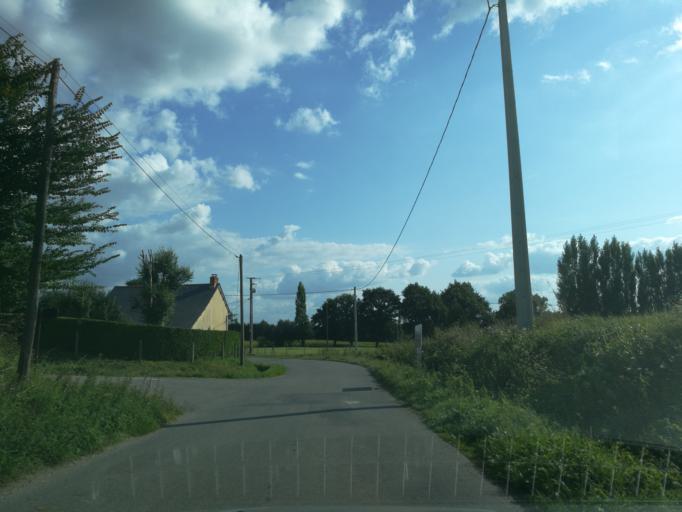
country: FR
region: Brittany
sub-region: Departement d'Ille-et-Vilaine
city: Bedee
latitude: 48.1894
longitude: -1.9554
